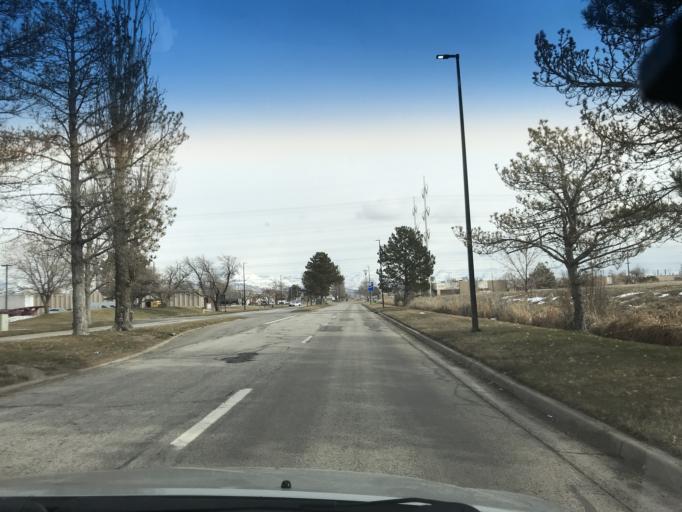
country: US
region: Utah
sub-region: Salt Lake County
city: West Valley City
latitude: 40.7763
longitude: -112.0085
